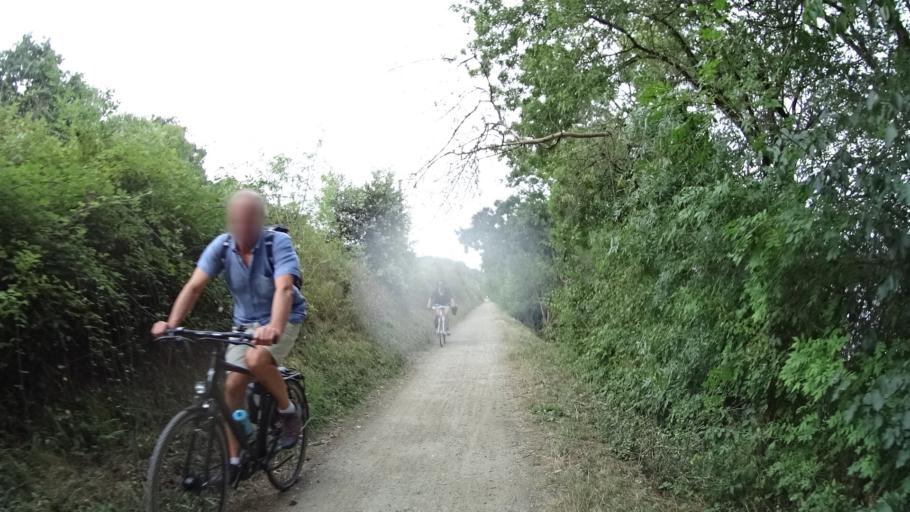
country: FR
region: Pays de la Loire
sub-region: Departement de Maine-et-Loire
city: La Varenne
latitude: 47.3288
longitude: -1.3250
